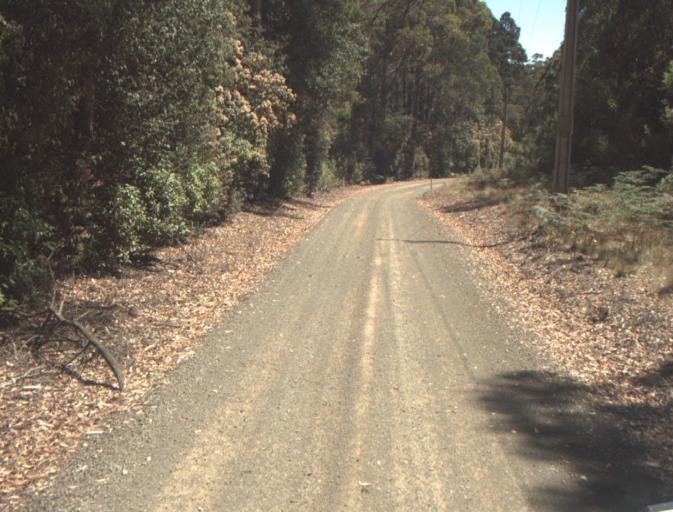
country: AU
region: Tasmania
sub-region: Dorset
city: Scottsdale
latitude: -41.3541
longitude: 147.3896
